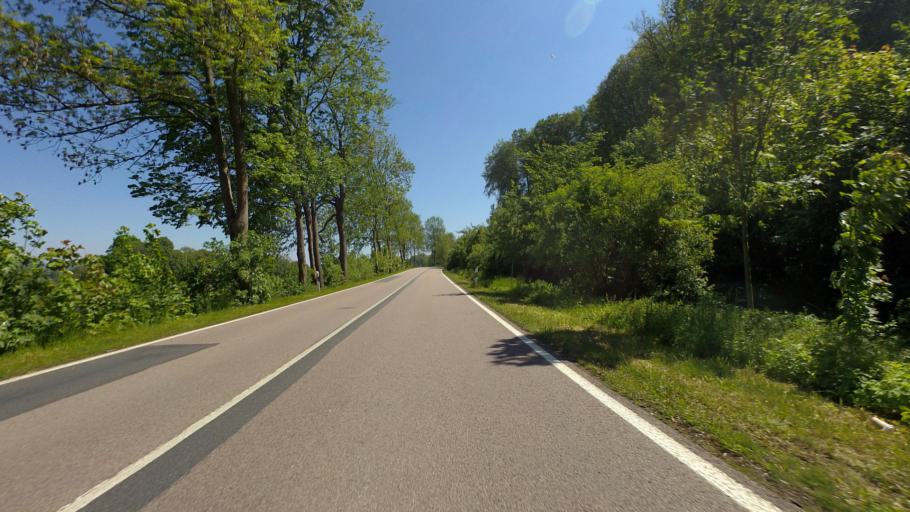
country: DE
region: Saxony
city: Klipphausen
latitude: 51.1208
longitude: 13.5404
